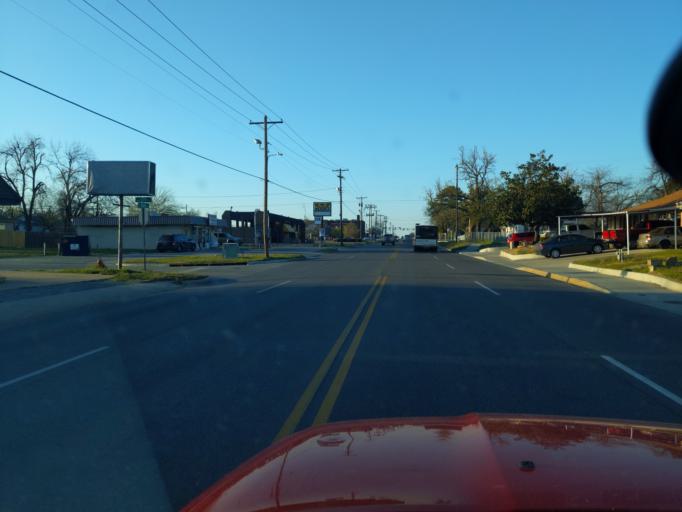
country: US
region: Oklahoma
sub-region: Oklahoma County
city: Oklahoma City
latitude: 35.4178
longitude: -97.5213
